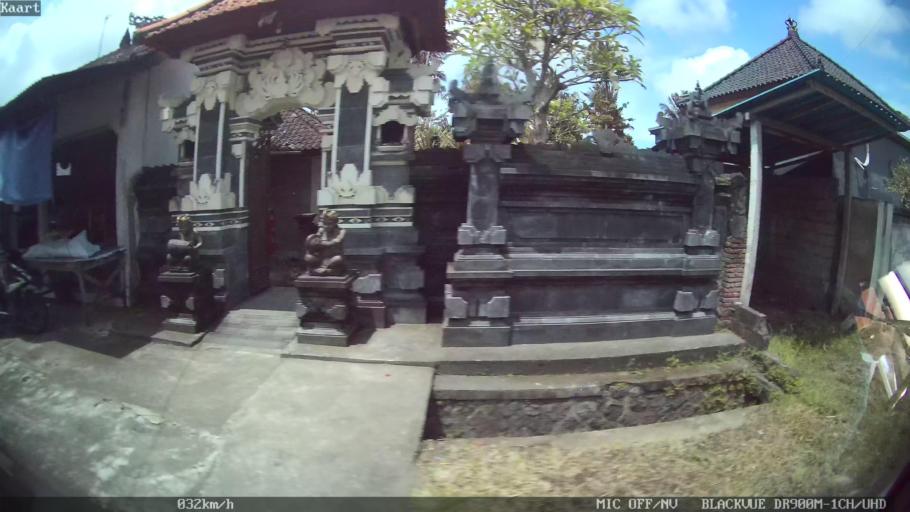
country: ID
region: Bali
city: Banjar Kelodan
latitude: -8.4833
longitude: 115.3678
